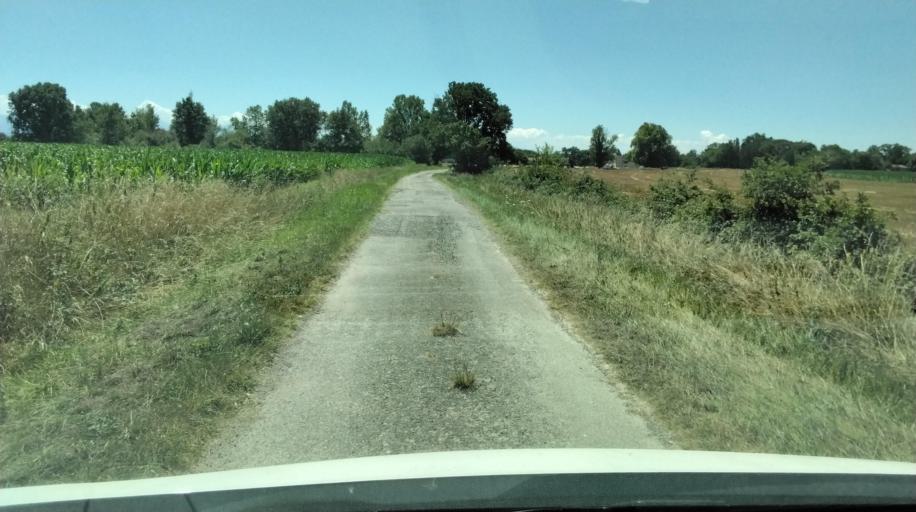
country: FR
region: Midi-Pyrenees
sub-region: Departement de la Haute-Garonne
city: Le Fousseret
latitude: 43.2740
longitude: 1.1265
